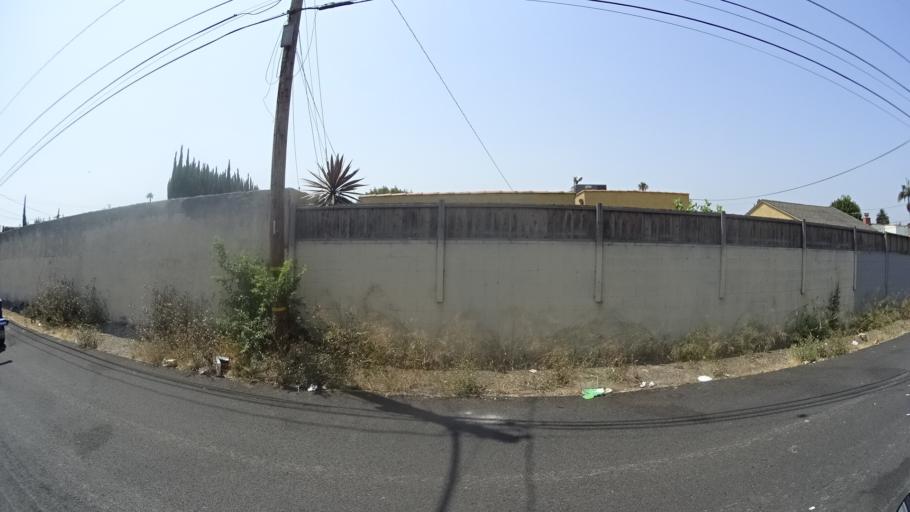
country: US
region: California
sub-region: Los Angeles County
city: Inglewood
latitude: 33.9727
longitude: -118.3337
